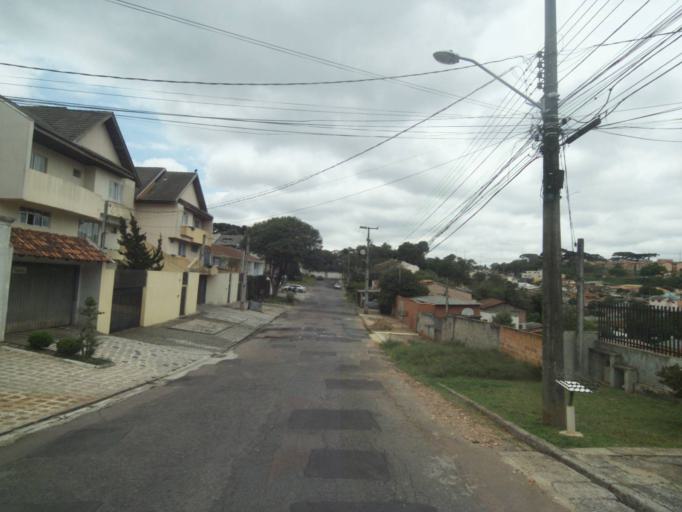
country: BR
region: Parana
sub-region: Curitiba
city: Curitiba
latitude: -25.3849
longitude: -49.2930
